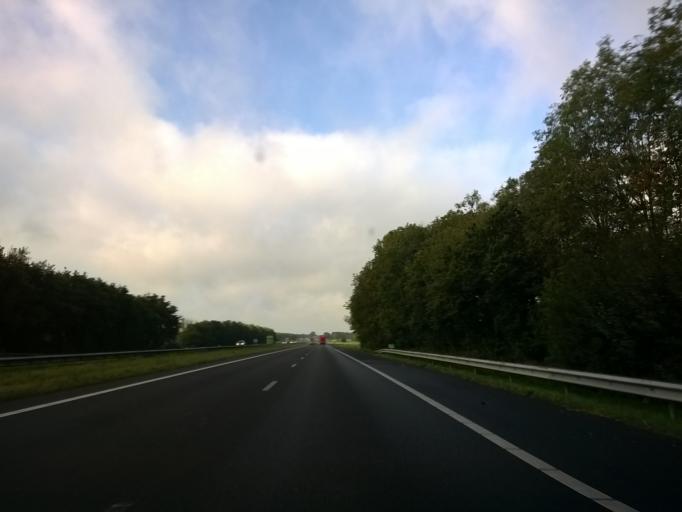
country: NL
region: Groningen
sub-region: Gemeente Grootegast
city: Grootegast
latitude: 53.1533
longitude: 6.2680
